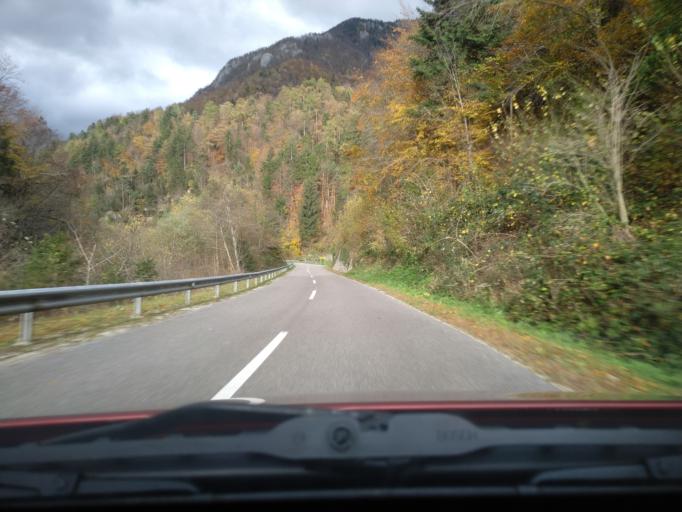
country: SI
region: Kamnik
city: Mekinje
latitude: 46.2853
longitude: 14.6171
